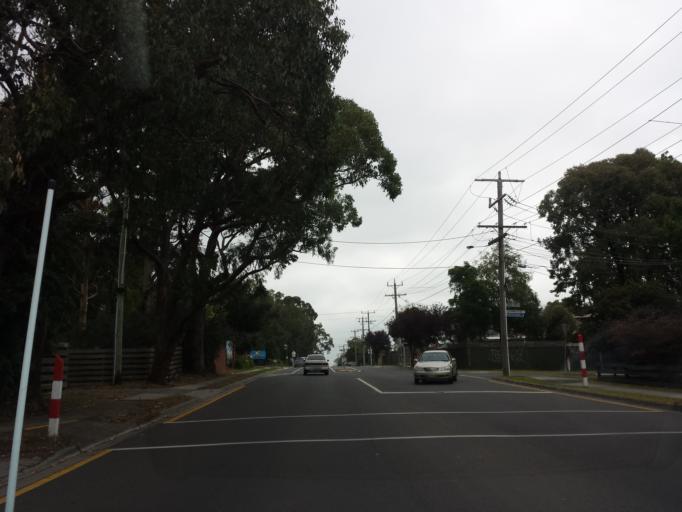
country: AU
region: Victoria
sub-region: Knox
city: The Basin
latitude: -37.8464
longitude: 145.2996
